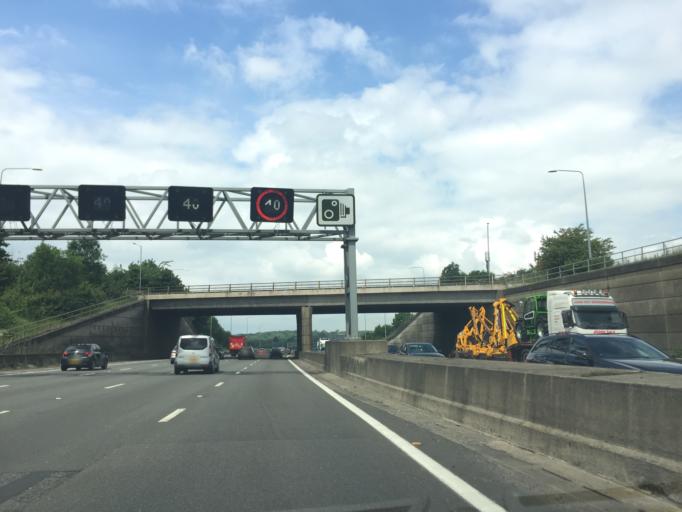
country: GB
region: England
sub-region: Buckinghamshire
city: Gerrards Cross
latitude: 51.5739
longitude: -0.5358
